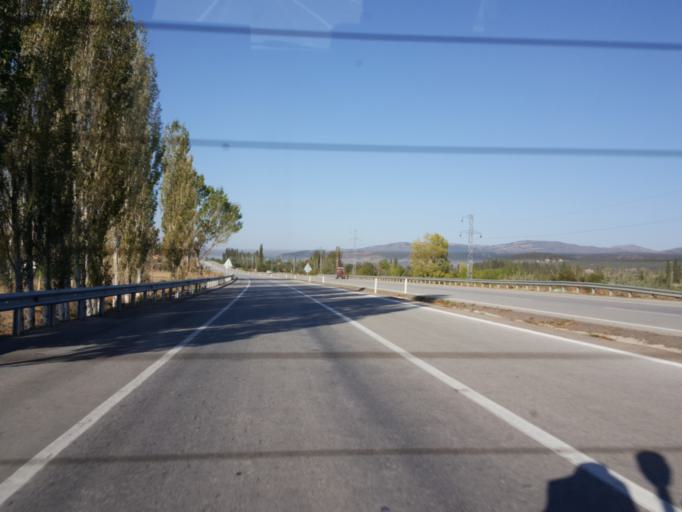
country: TR
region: Amasya
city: Ezinepazari
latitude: 40.5723
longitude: 36.1181
